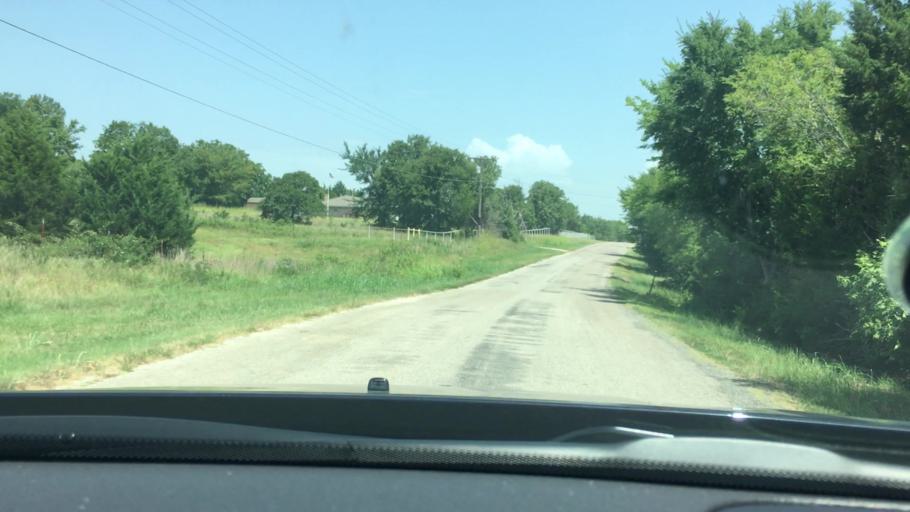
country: US
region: Oklahoma
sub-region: Pontotoc County
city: Byng
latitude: 34.8281
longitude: -96.6698
